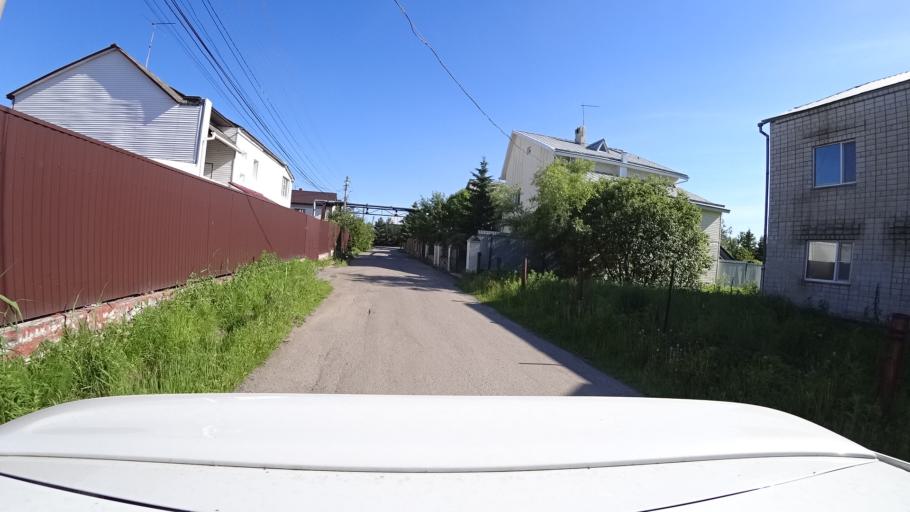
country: RU
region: Khabarovsk Krai
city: Topolevo
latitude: 48.5423
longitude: 135.1766
